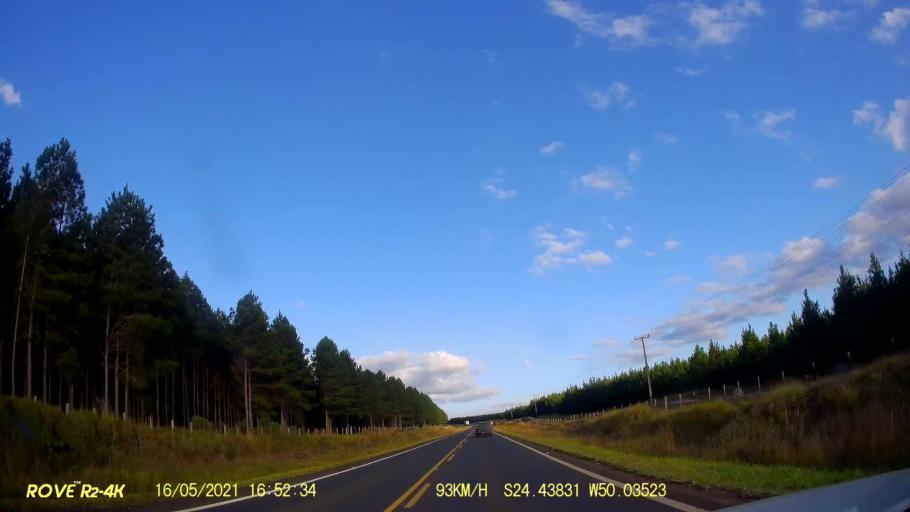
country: BR
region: Parana
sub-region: Pirai Do Sul
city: Pirai do Sul
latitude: -24.4383
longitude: -50.0352
